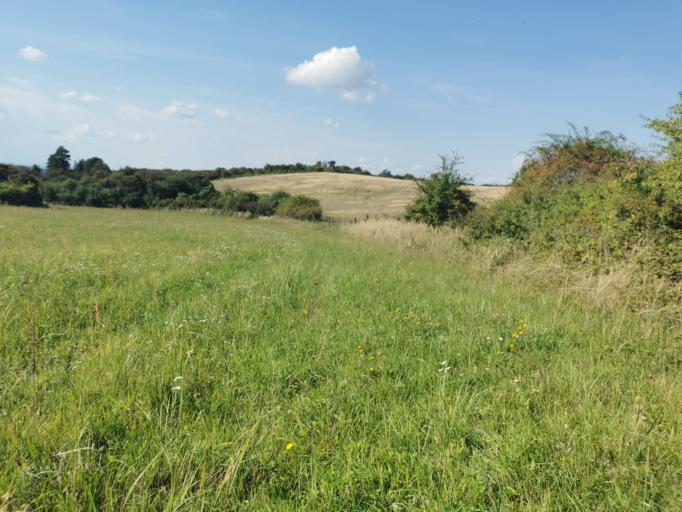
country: SK
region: Trnavsky
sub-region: Okres Senica
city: Senica
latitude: 48.6049
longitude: 17.2354
